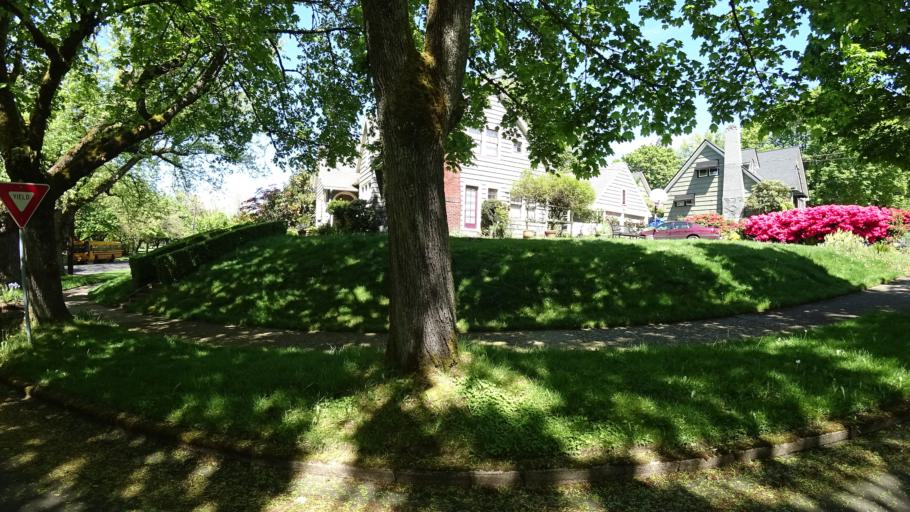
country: US
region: Oregon
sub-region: Clackamas County
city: Milwaukie
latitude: 45.4686
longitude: -122.6353
